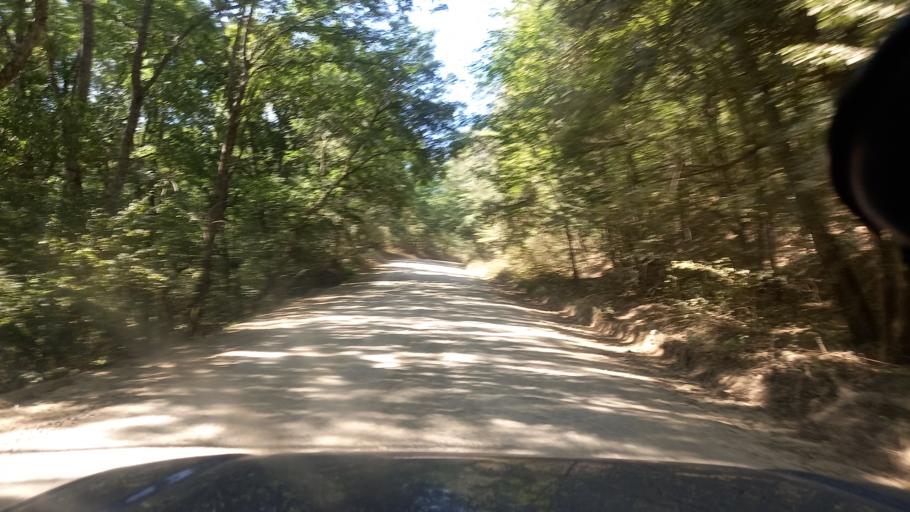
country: RU
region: Krasnodarskiy
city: Azovskaya
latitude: 44.6972
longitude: 38.6562
